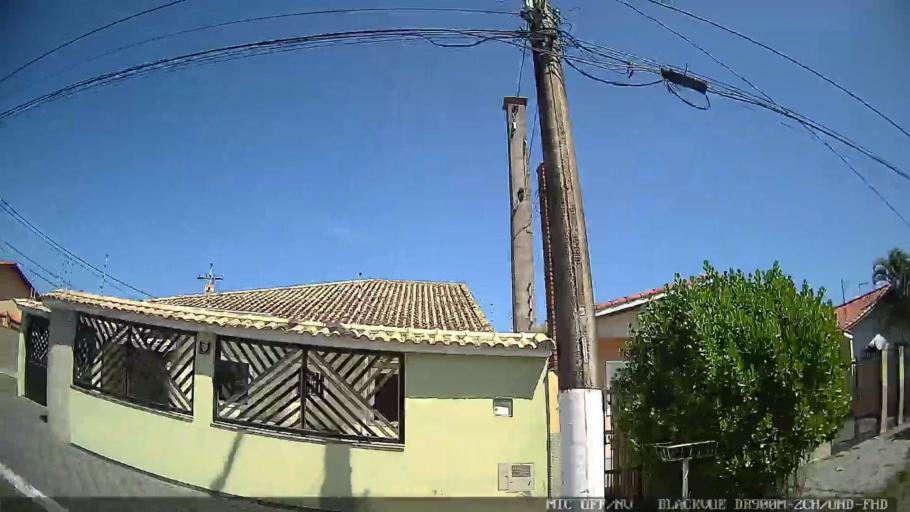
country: BR
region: Sao Paulo
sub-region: Peruibe
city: Peruibe
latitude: -24.3024
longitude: -46.9800
